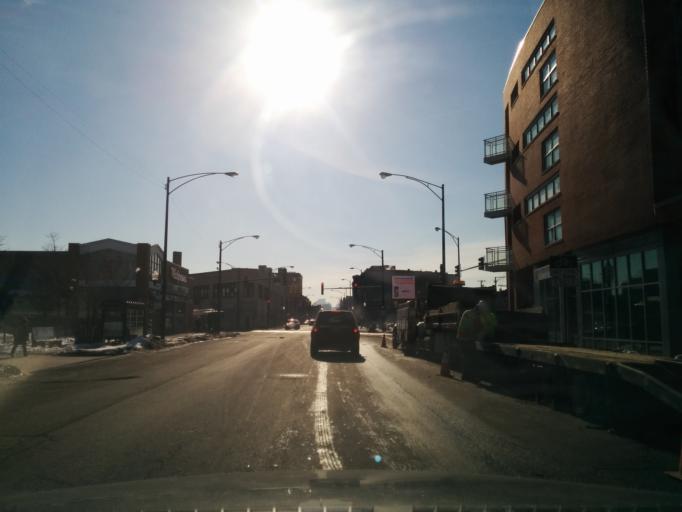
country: US
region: Illinois
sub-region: Cook County
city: Chicago
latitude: 41.9180
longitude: -87.6894
